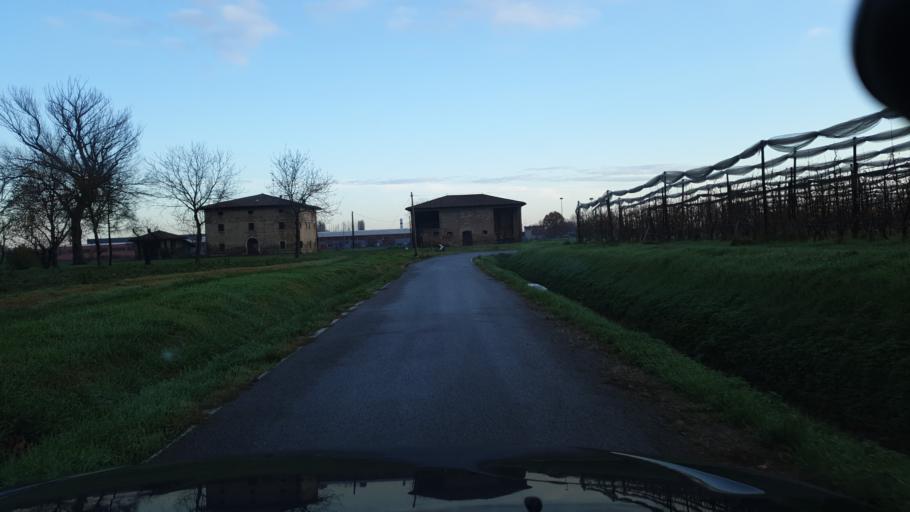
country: IT
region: Emilia-Romagna
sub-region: Provincia di Bologna
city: Crespellano
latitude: 44.5212
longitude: 11.1437
